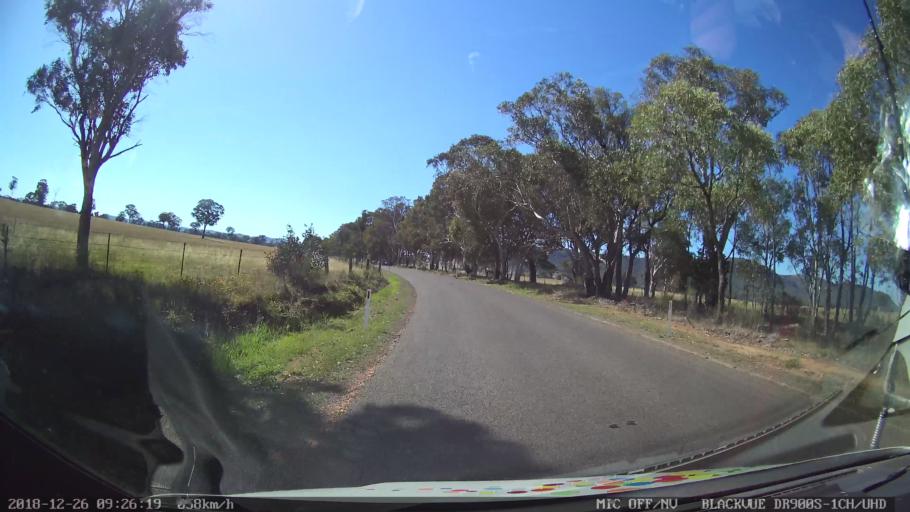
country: AU
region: New South Wales
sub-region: Mid-Western Regional
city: Kandos
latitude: -32.8277
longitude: 150.0074
